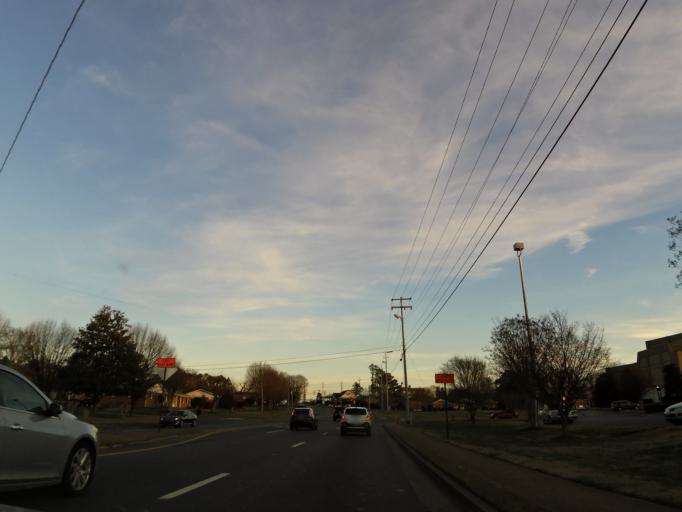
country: US
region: Tennessee
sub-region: Bradley County
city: Cleveland
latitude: 35.1816
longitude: -84.8718
